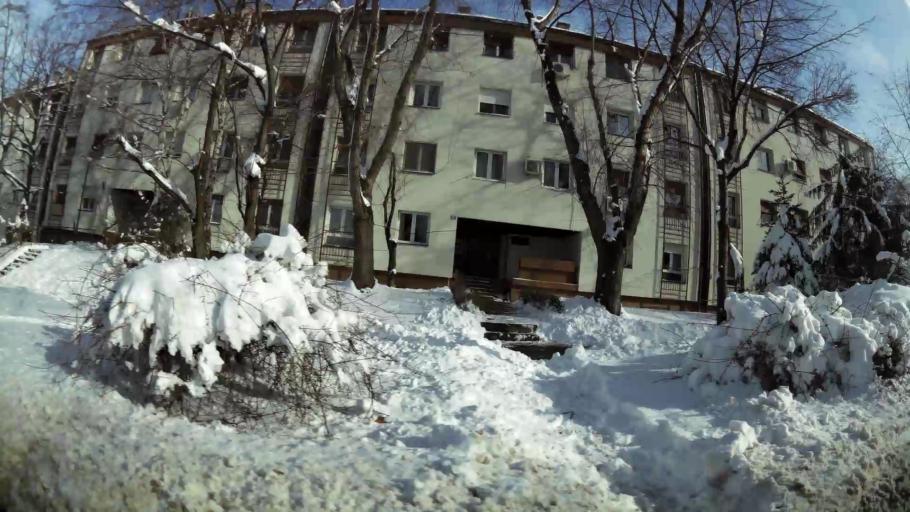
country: RS
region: Central Serbia
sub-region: Belgrade
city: Zvezdara
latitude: 44.7949
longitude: 20.5357
